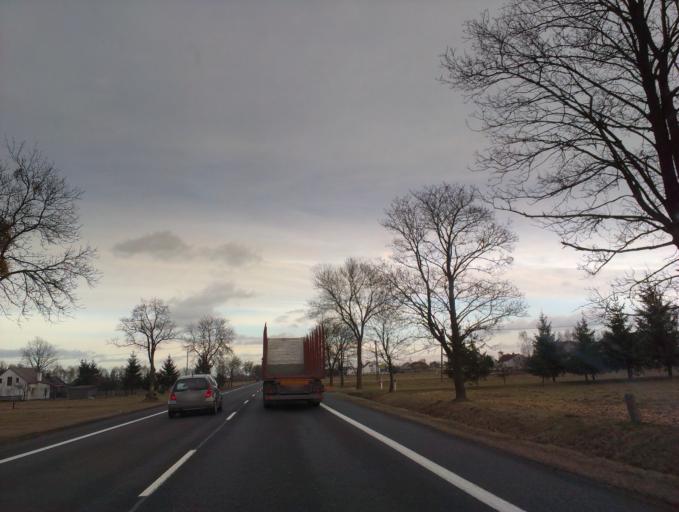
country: PL
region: Masovian Voivodeship
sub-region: Powiat sierpecki
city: Szczutowo
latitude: 52.9034
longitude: 19.5035
